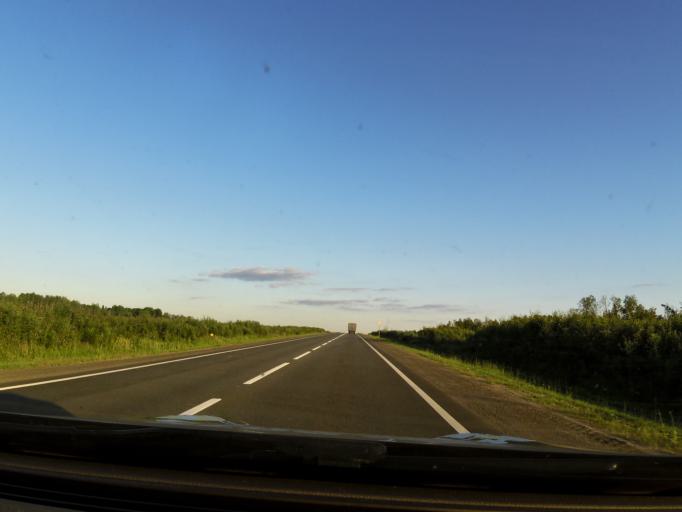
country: RU
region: Jaroslavl
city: Prechistoye
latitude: 58.6536
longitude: 40.3182
